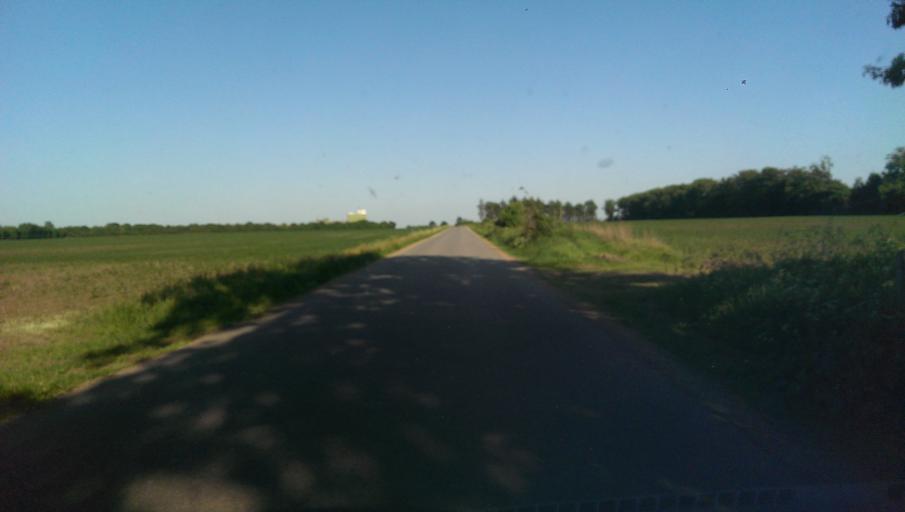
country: DK
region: South Denmark
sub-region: Esbjerg Kommune
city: Bramming
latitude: 55.5499
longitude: 8.6430
